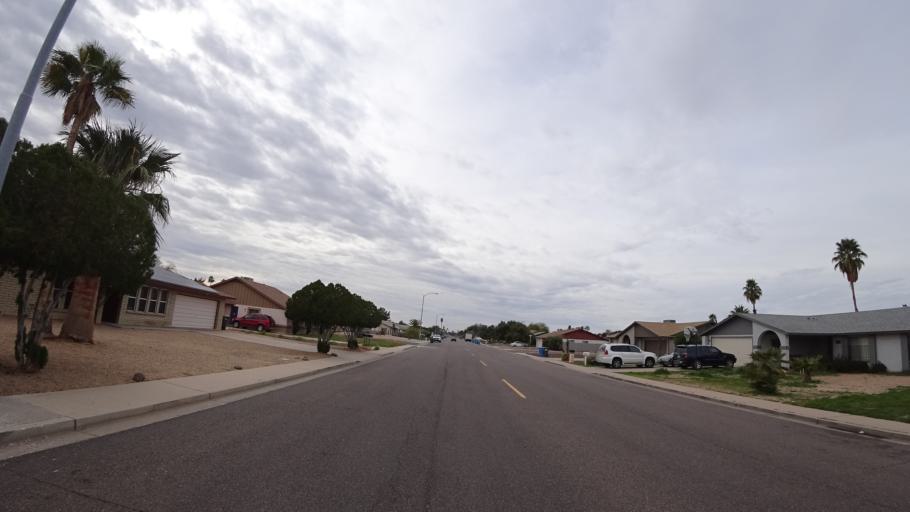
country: US
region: Arizona
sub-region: Maricopa County
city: Glendale
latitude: 33.6473
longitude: -112.1377
